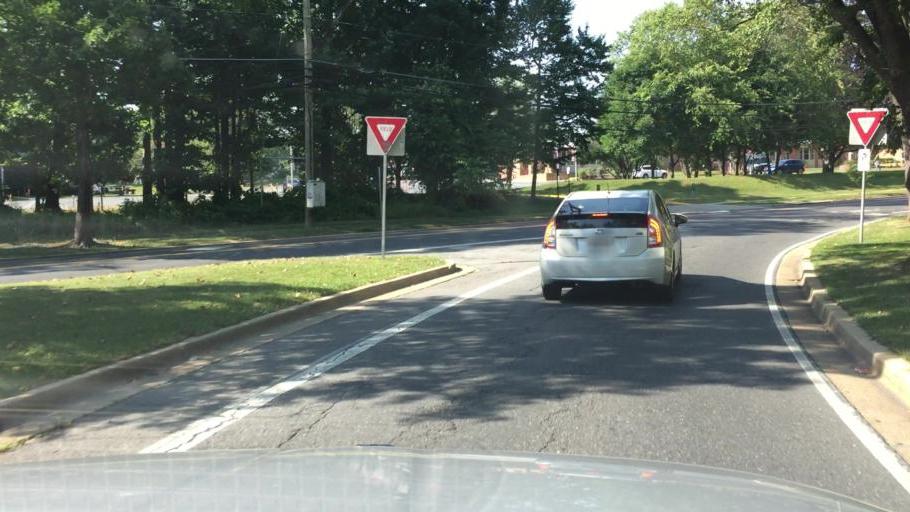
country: US
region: Maryland
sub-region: Montgomery County
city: Kemp Mill
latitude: 39.0459
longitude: -77.0315
